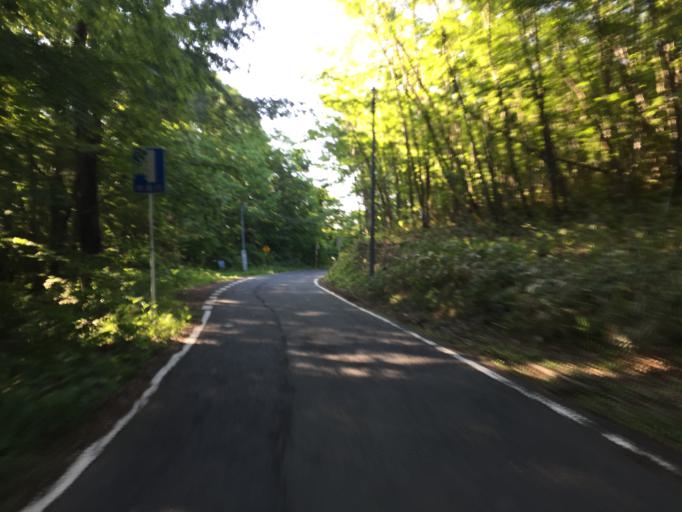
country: JP
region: Ibaraki
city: Kitaibaraki
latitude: 36.9053
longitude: 140.5878
